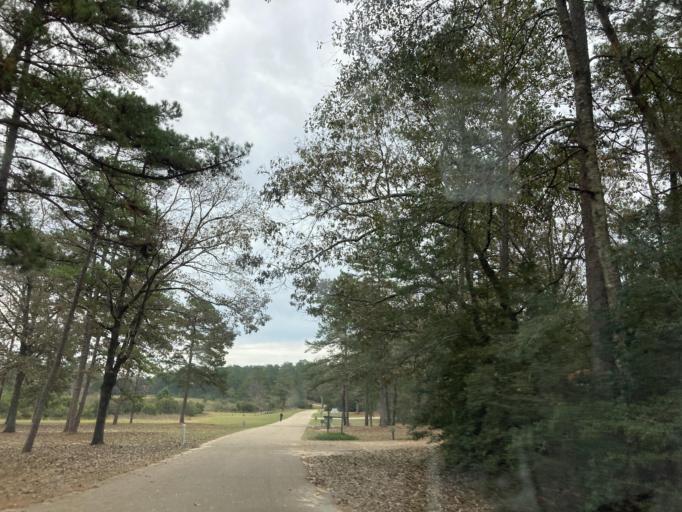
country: US
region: Mississippi
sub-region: Lamar County
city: Lumberton
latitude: 31.0816
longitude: -89.4938
